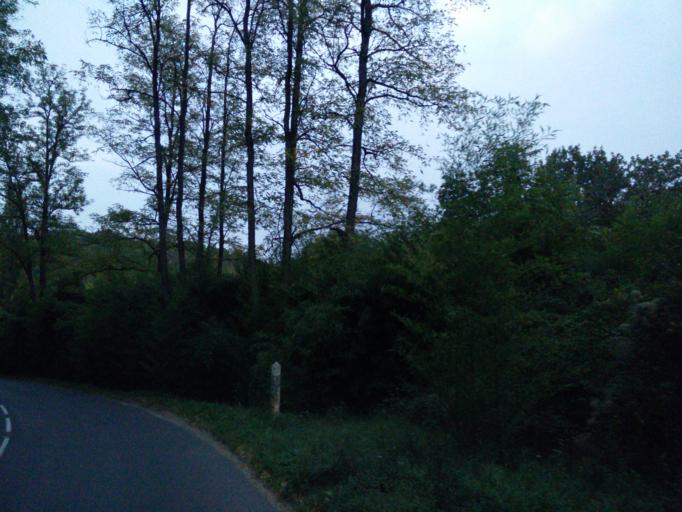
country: FR
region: Aquitaine
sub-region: Departement de la Dordogne
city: Carsac-Aillac
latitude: 44.8599
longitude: 1.2510
